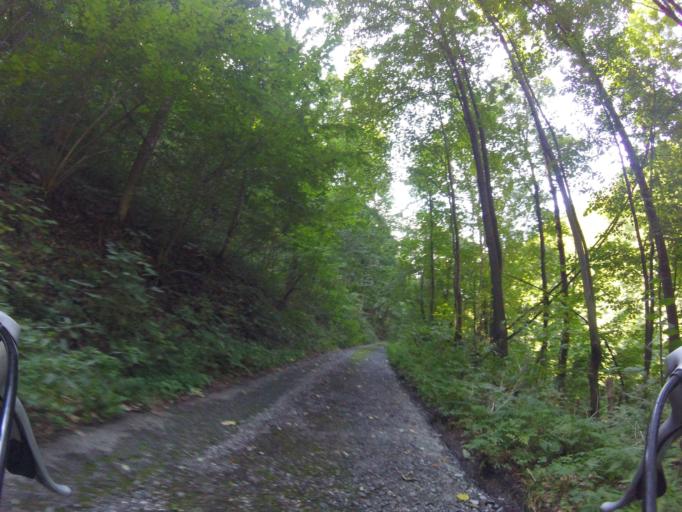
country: HU
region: Heves
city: Szilvasvarad
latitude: 48.1127
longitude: 20.5522
